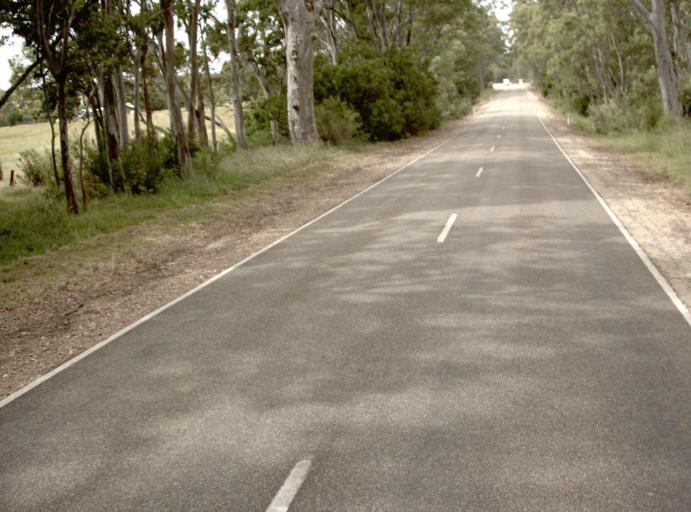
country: AU
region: Victoria
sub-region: Wellington
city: Sale
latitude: -37.9235
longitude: 147.0875
